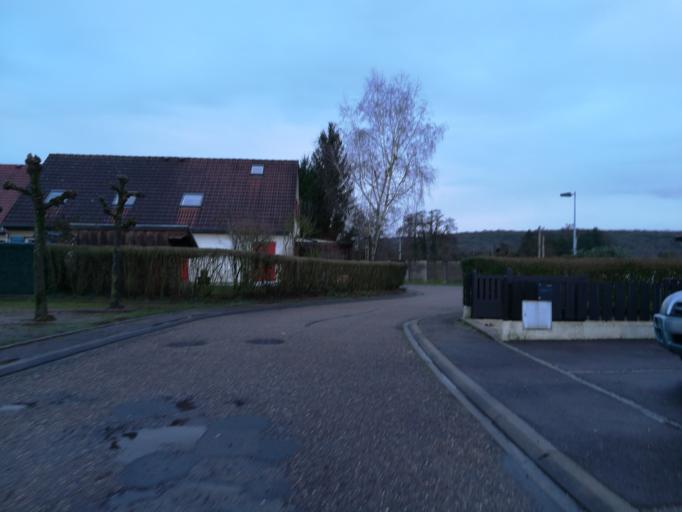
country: FR
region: Lorraine
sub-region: Departement de la Moselle
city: Ars-sur-Moselle
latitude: 49.0738
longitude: 6.0758
